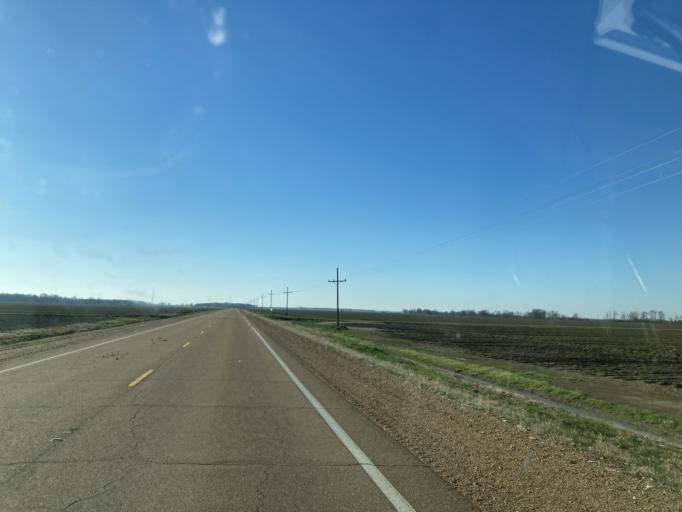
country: US
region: Mississippi
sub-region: Yazoo County
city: Yazoo City
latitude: 32.9534
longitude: -90.5842
